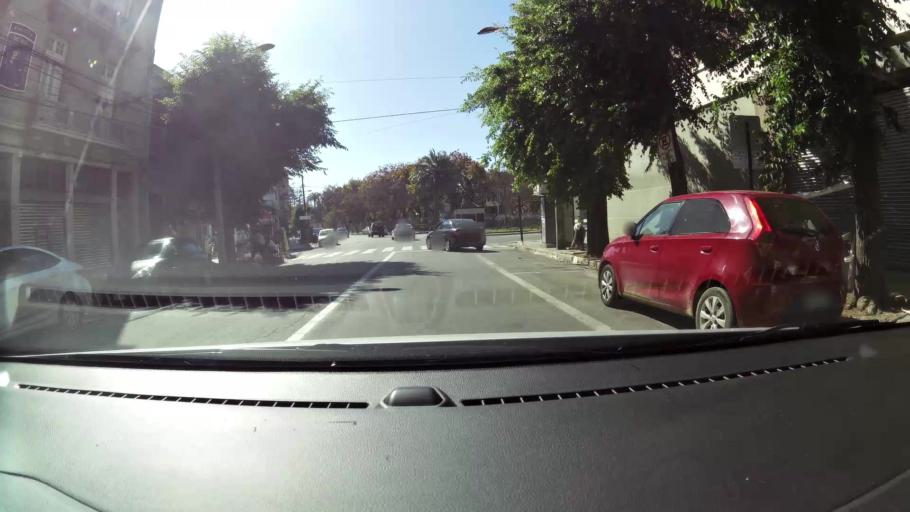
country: CL
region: Valparaiso
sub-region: Provincia de Valparaiso
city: Valparaiso
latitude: -33.0492
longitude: -71.6050
